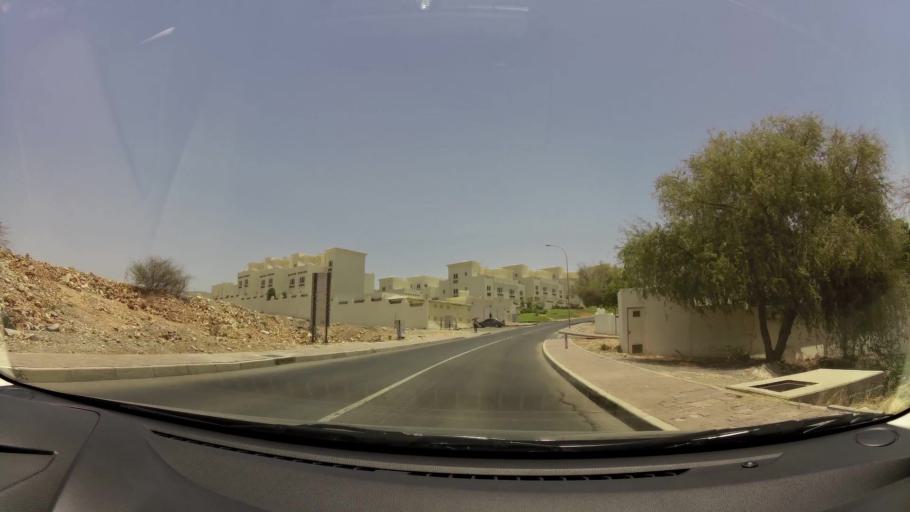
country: OM
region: Muhafazat Masqat
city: Bawshar
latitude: 23.6046
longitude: 58.4866
